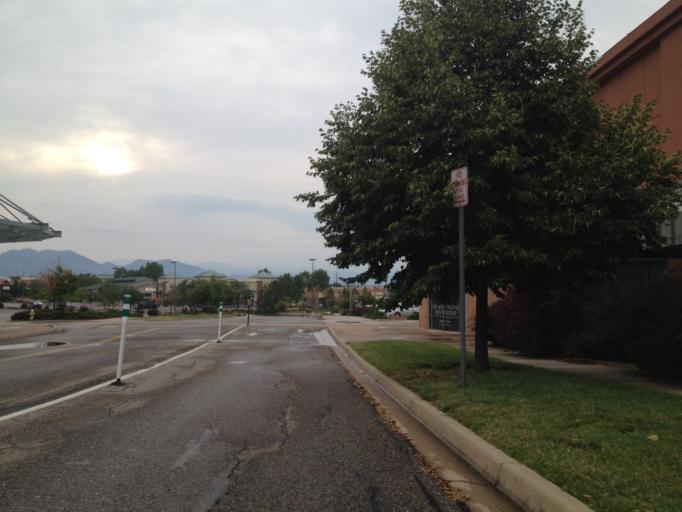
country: US
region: Colorado
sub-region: Broomfield County
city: Broomfield
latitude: 39.9302
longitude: -105.1213
